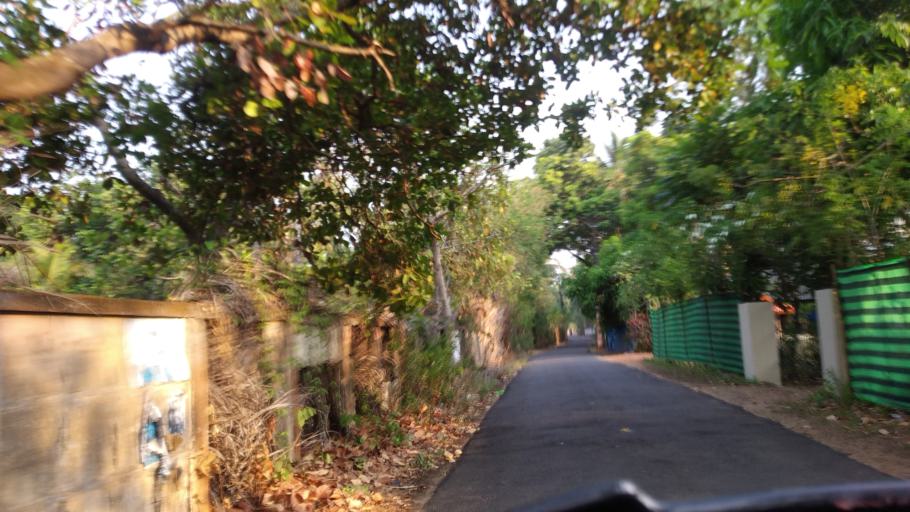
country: IN
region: Kerala
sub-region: Thrissur District
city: Thanniyam
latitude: 10.4308
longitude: 76.0796
